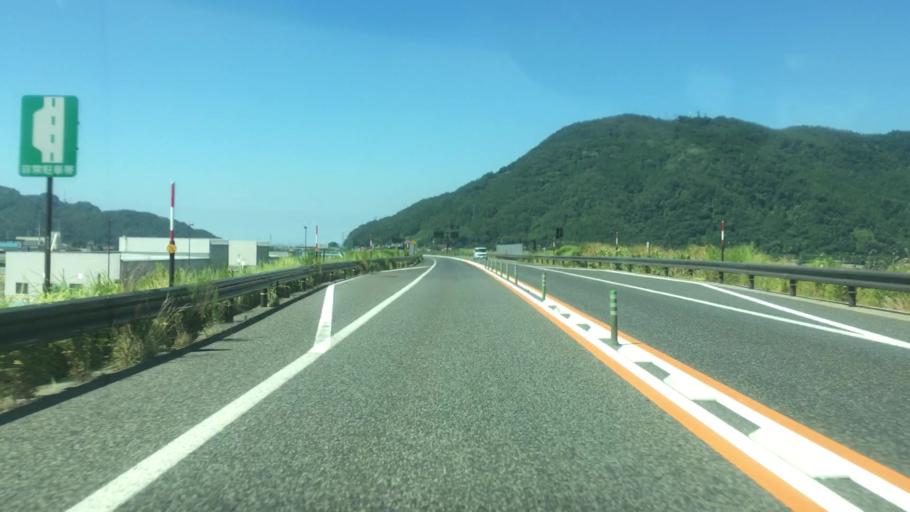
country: JP
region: Tottori
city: Tottori
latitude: 35.3954
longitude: 134.2043
